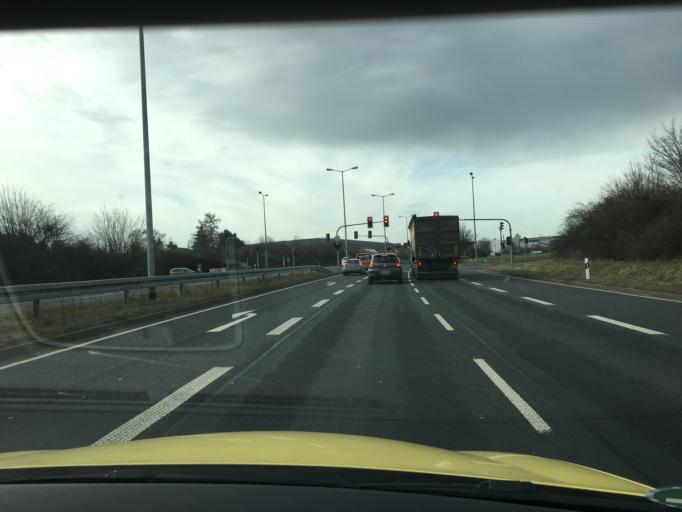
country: DE
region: Thuringia
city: Erfurt
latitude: 50.9625
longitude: 11.0887
